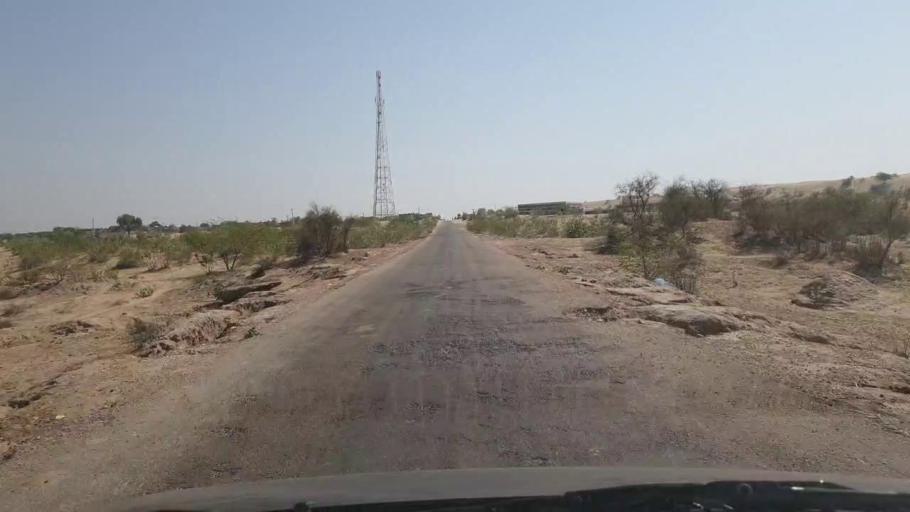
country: PK
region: Sindh
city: Chor
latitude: 25.6009
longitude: 69.9927
